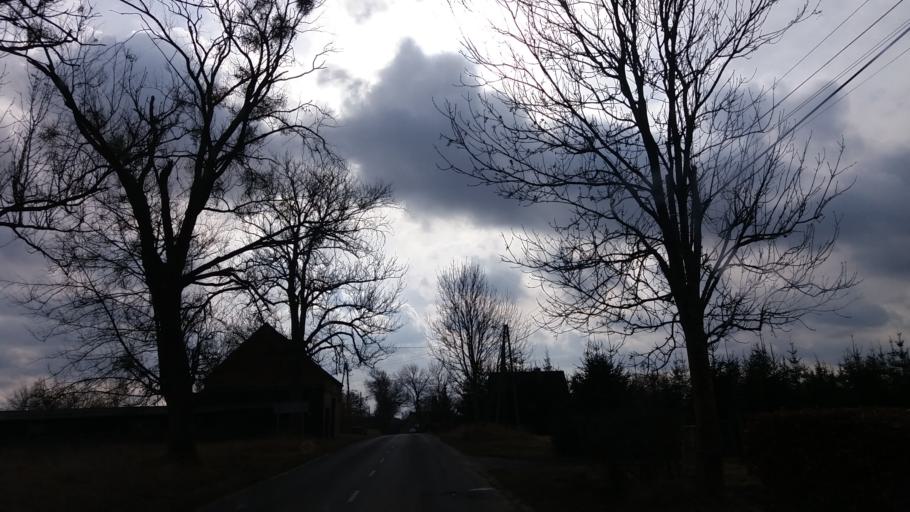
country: PL
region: West Pomeranian Voivodeship
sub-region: Powiat choszczenski
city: Drawno
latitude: 53.2250
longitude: 15.7534
